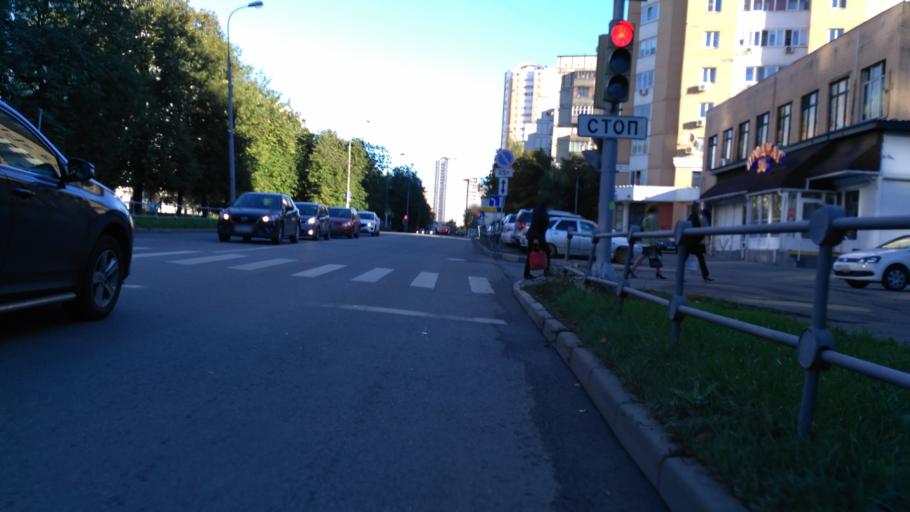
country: RU
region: Moskovskaya
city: Vostochnoe Degunino
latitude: 55.8675
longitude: 37.5580
